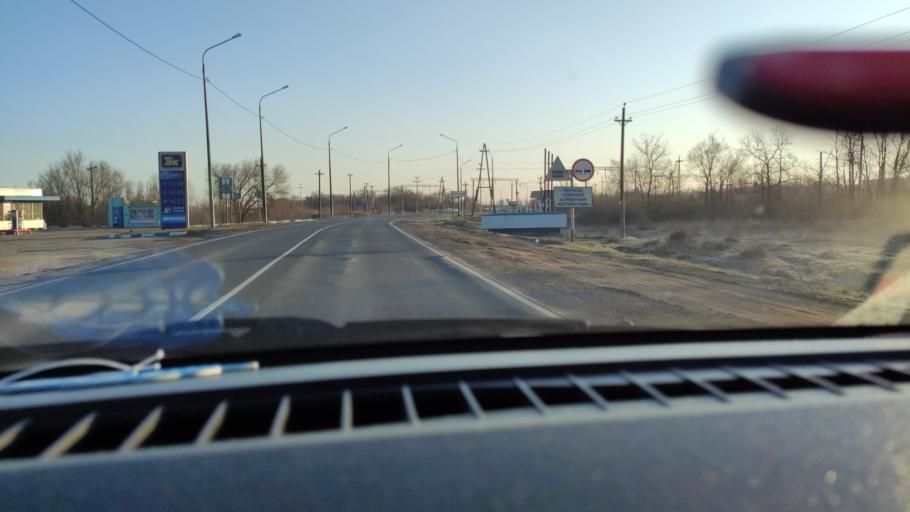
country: RU
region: Saratov
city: Sennoy
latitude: 52.1501
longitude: 46.9483
